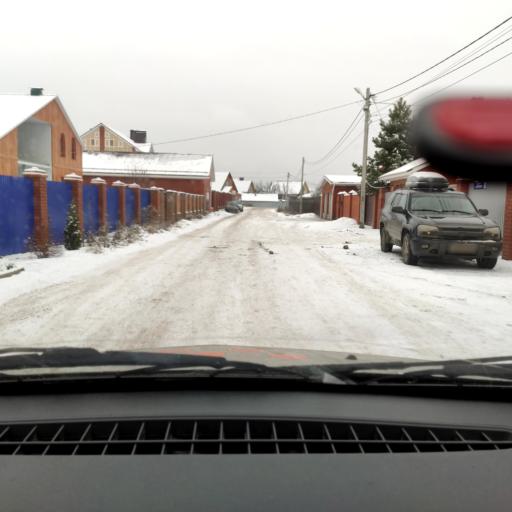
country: RU
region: Bashkortostan
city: Mikhaylovka
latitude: 54.8086
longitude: 55.9398
